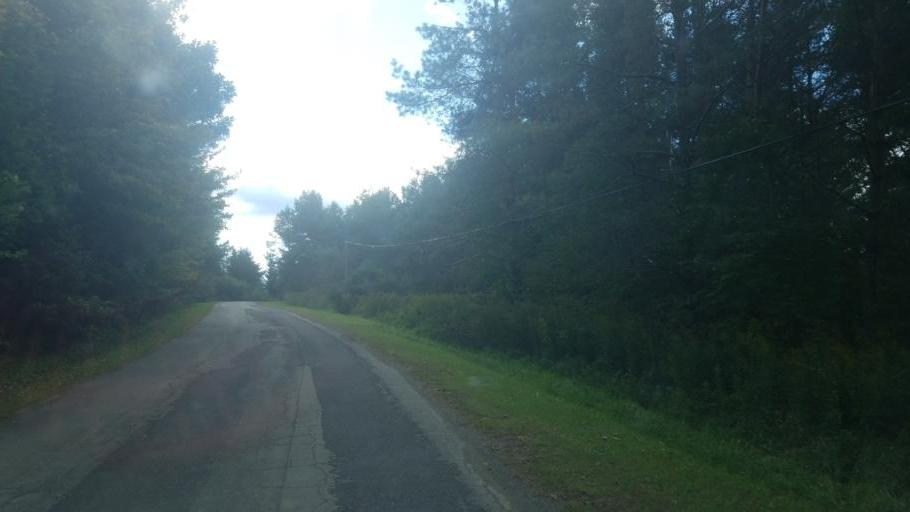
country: US
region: New York
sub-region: Cattaraugus County
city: Franklinville
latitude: 42.2244
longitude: -78.4154
